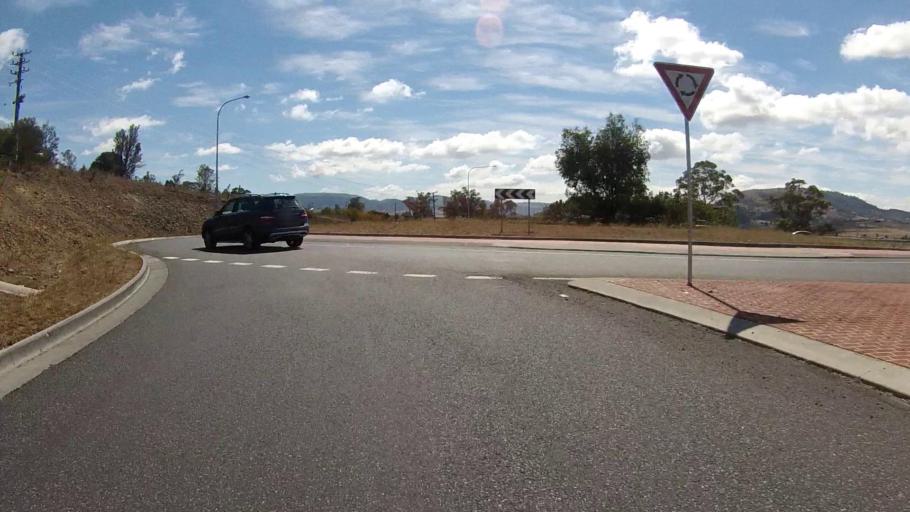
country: AU
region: Tasmania
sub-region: Brighton
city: Bridgewater
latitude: -42.7129
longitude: 147.2429
